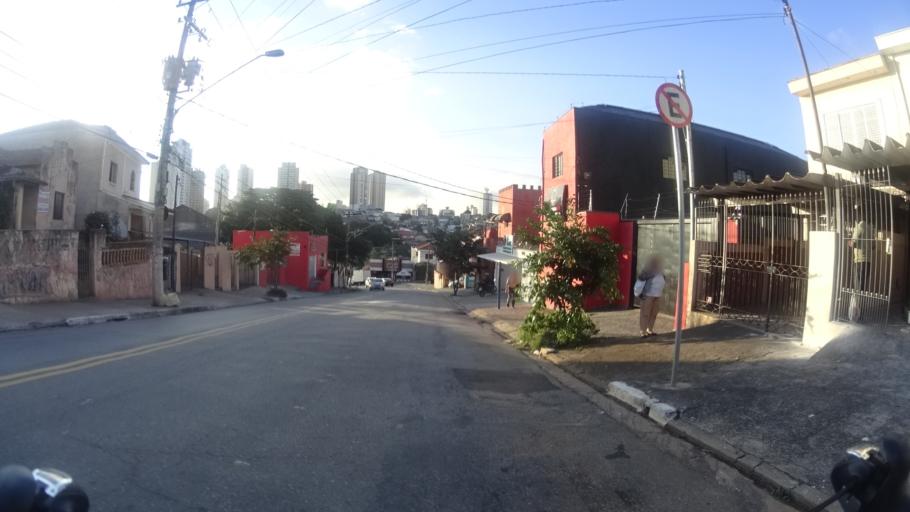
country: BR
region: Sao Paulo
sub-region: Sao Paulo
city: Sao Paulo
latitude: -23.4874
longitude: -46.6385
